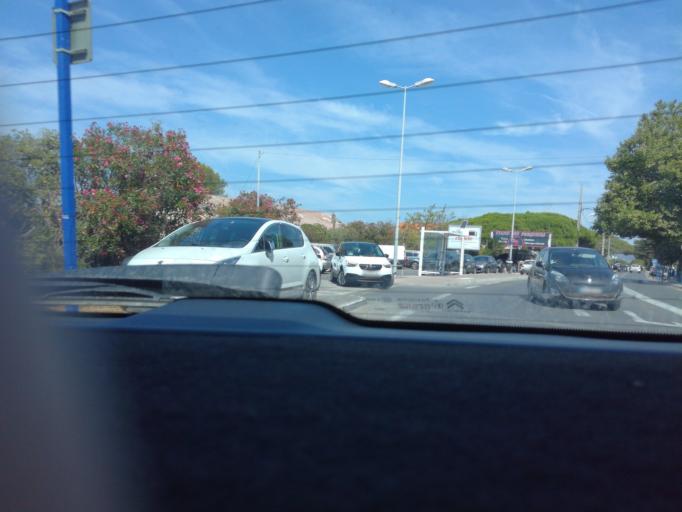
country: FR
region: Provence-Alpes-Cote d'Azur
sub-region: Departement du Var
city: Hyeres
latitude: 43.0653
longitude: 6.1472
